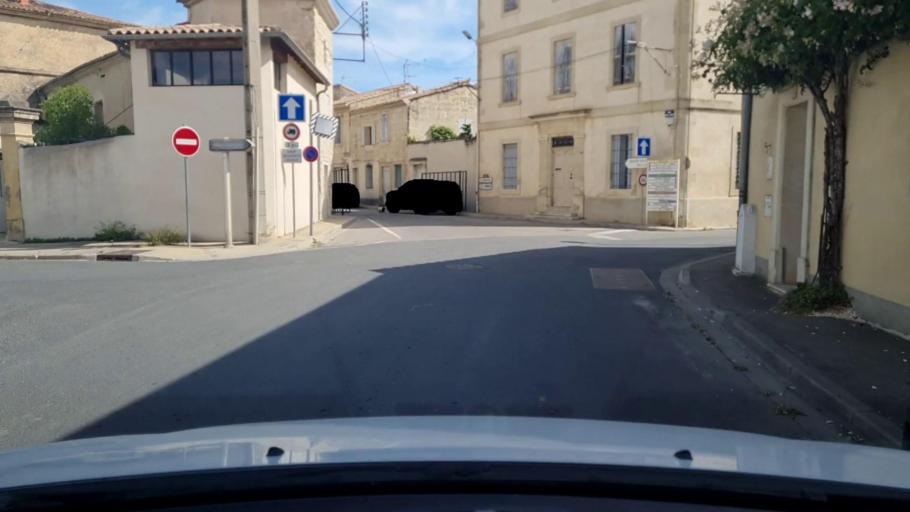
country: FR
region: Languedoc-Roussillon
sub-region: Departement de l'Herault
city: Marsillargues
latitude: 43.6323
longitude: 4.1971
